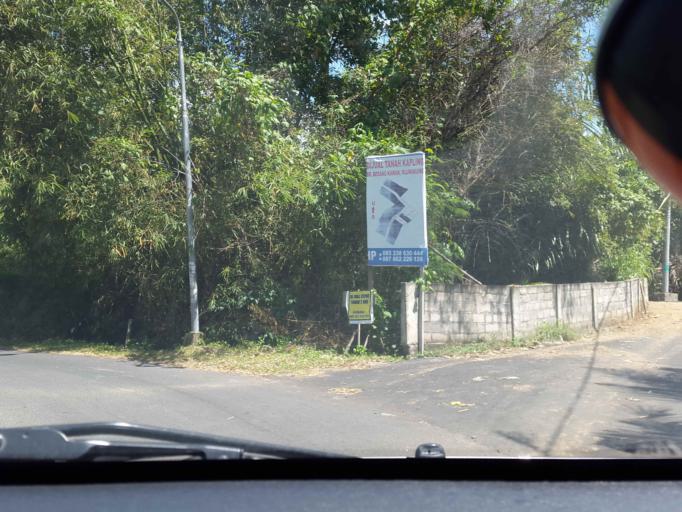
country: ID
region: Bali
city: Klungkung
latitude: -8.5201
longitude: 115.3960
